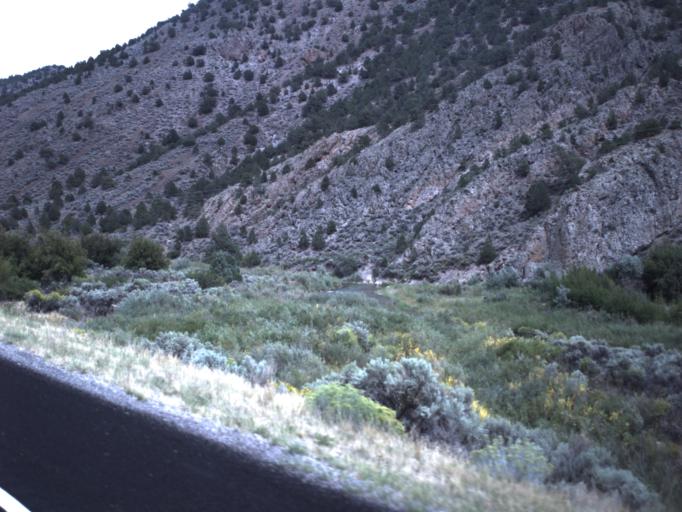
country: US
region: Utah
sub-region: Piute County
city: Junction
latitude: 38.0891
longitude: -112.3387
